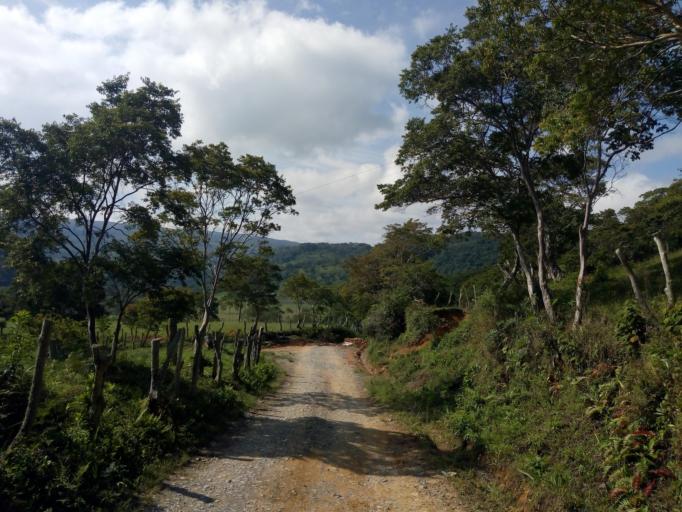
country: CO
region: Boyaca
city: Moniquira
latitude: 5.8821
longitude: -73.5080
